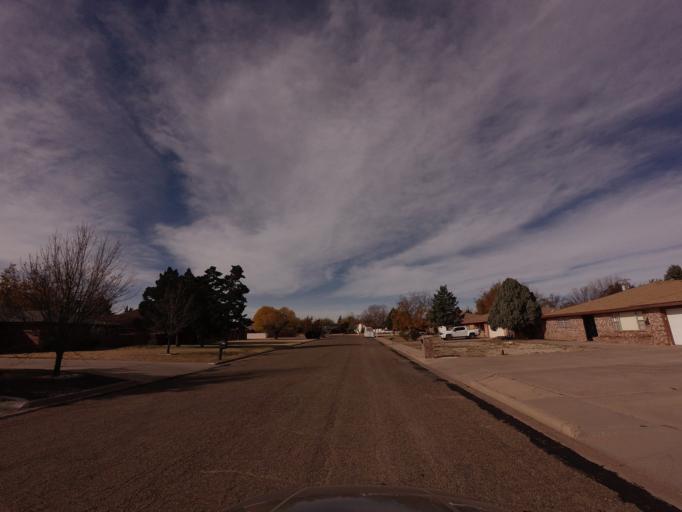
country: US
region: New Mexico
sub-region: Curry County
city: Clovis
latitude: 34.4171
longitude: -103.1884
